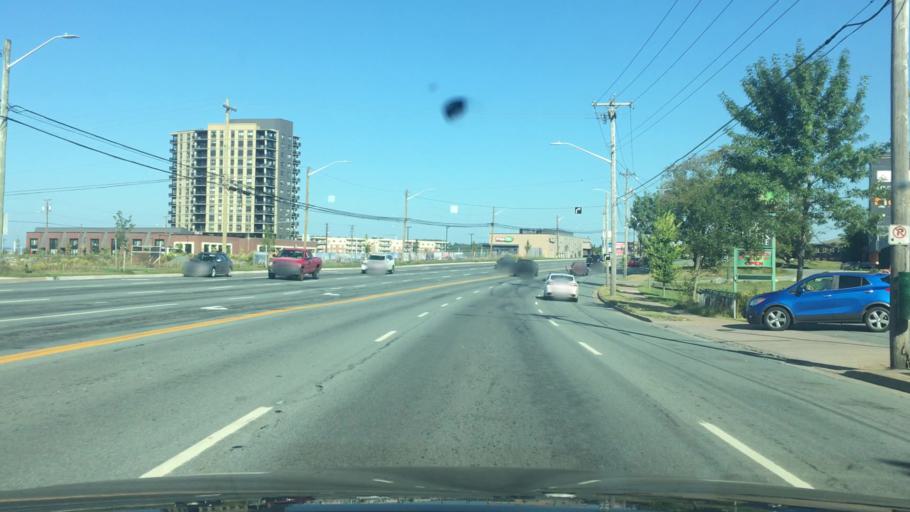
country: CA
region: Nova Scotia
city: Dartmouth
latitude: 44.6986
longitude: -63.6052
